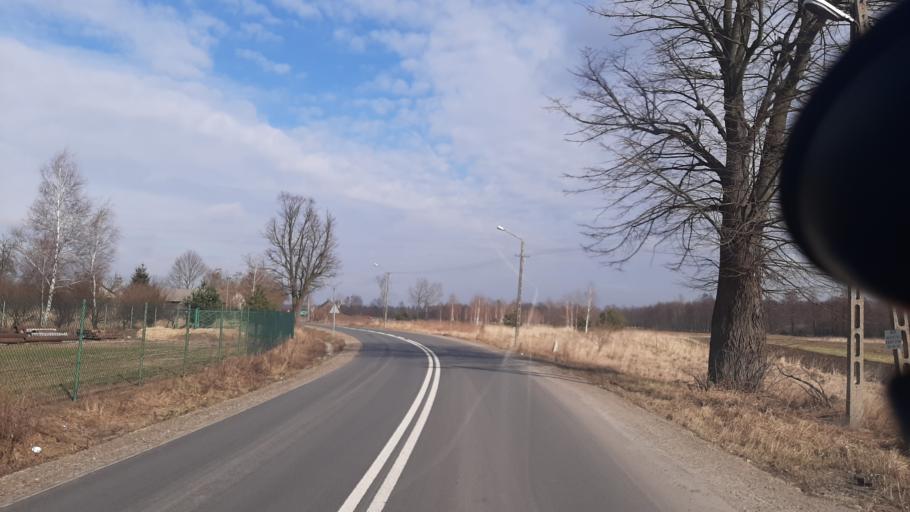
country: PL
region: Lublin Voivodeship
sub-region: Powiat lubartowski
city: Serniki
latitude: 51.4379
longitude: 22.6597
